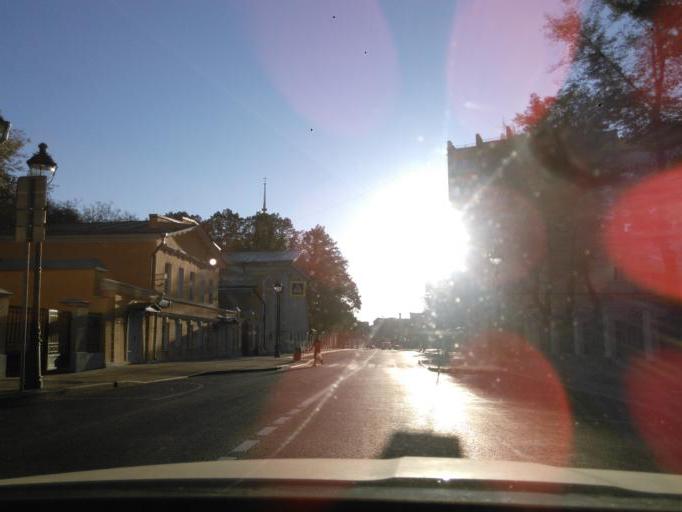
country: RU
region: Moscow
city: Moscow
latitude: 55.7577
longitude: 37.5917
